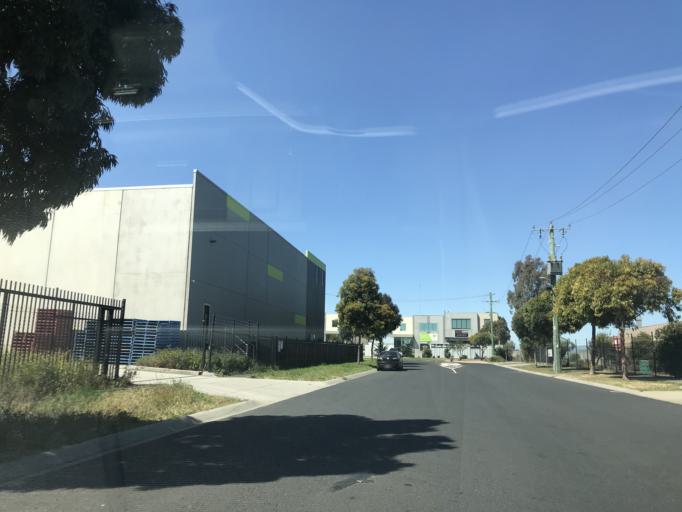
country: AU
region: Victoria
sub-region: Wyndham
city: Truganina
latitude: -37.8248
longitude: 144.7704
